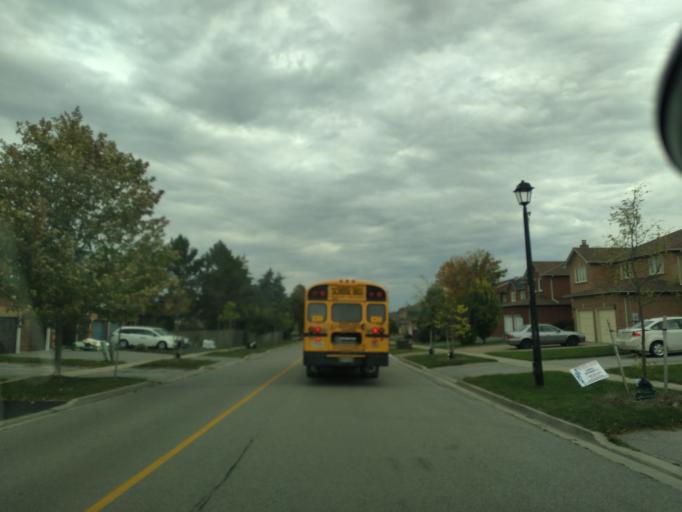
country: CA
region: Ontario
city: Newmarket
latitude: 44.0282
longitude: -79.4725
